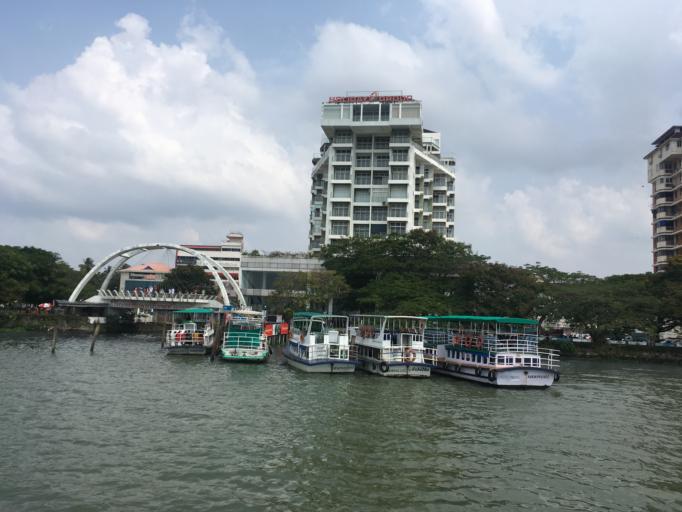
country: IN
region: Kerala
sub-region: Ernakulam
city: Cochin
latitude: 9.9792
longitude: 76.2745
